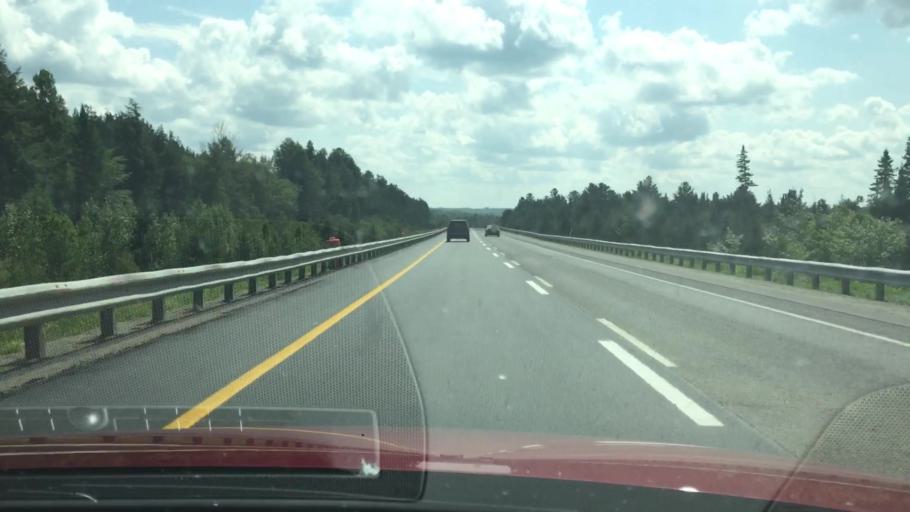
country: US
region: Maine
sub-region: Penobscot County
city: Medway
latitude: 45.6505
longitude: -68.4995
